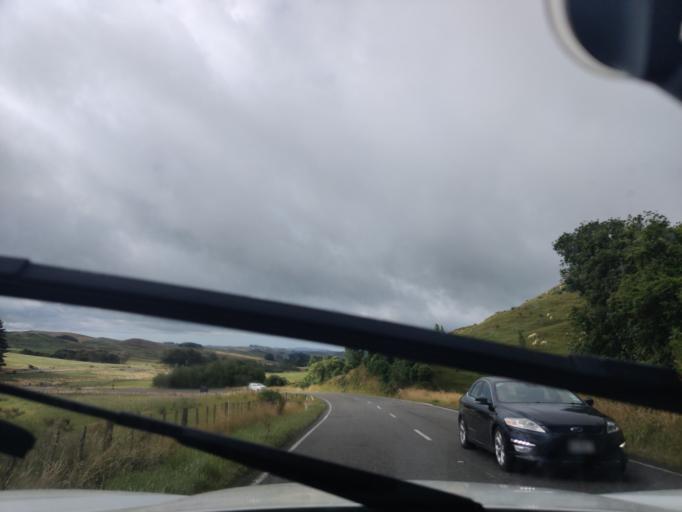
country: NZ
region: Manawatu-Wanganui
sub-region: Palmerston North City
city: Palmerston North
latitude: -40.4216
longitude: 175.7396
